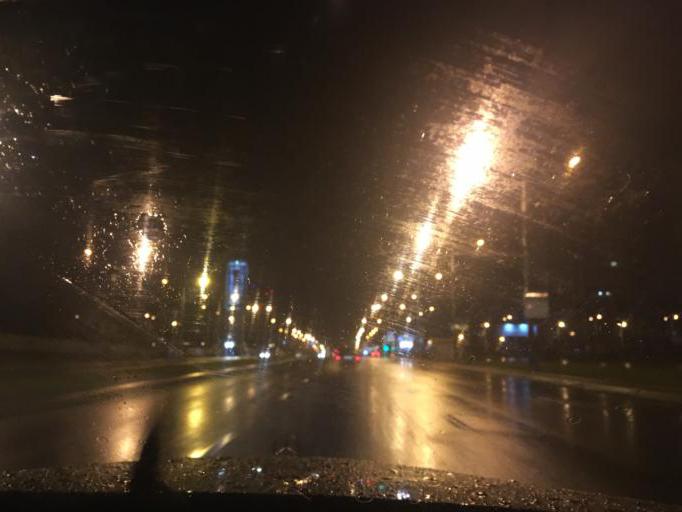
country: BY
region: Minsk
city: Minsk
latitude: 53.8856
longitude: 27.5120
